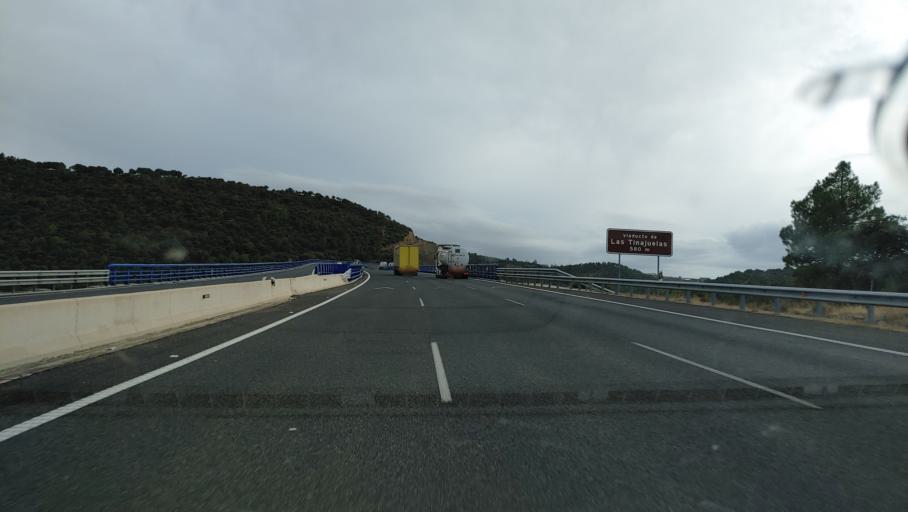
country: ES
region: Andalusia
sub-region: Provincia de Jaen
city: Santa Elena
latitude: 38.3643
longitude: -3.5238
